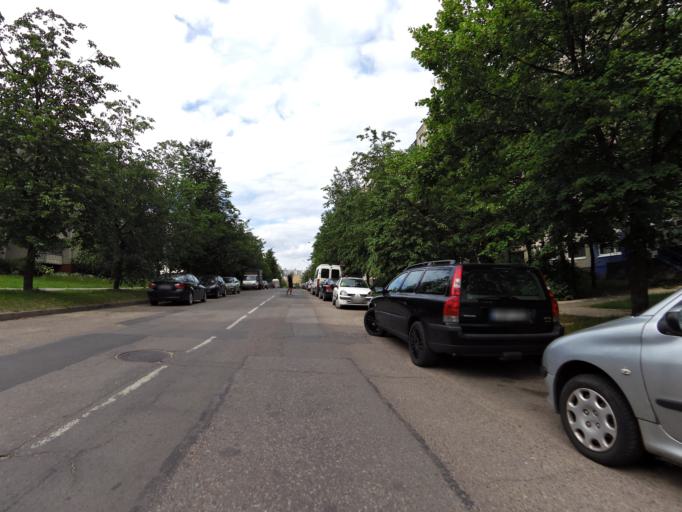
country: LT
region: Vilnius County
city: Seskine
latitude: 54.7175
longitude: 25.2375
